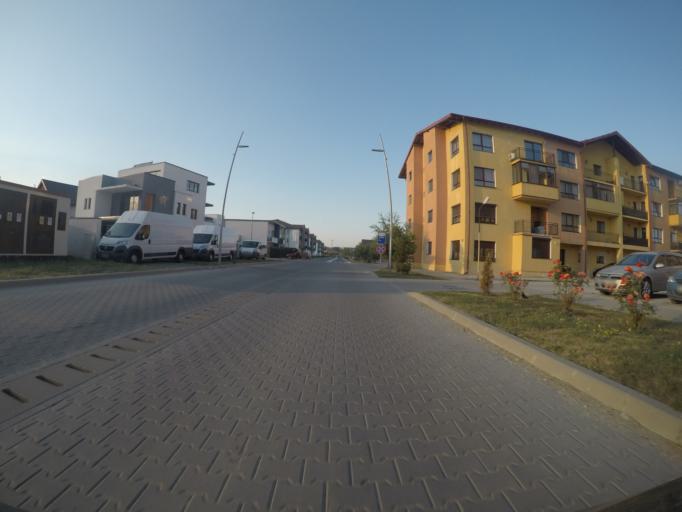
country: RO
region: Sibiu
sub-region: Comuna Selimbar
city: Selimbar
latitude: 45.7821
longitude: 24.1819
